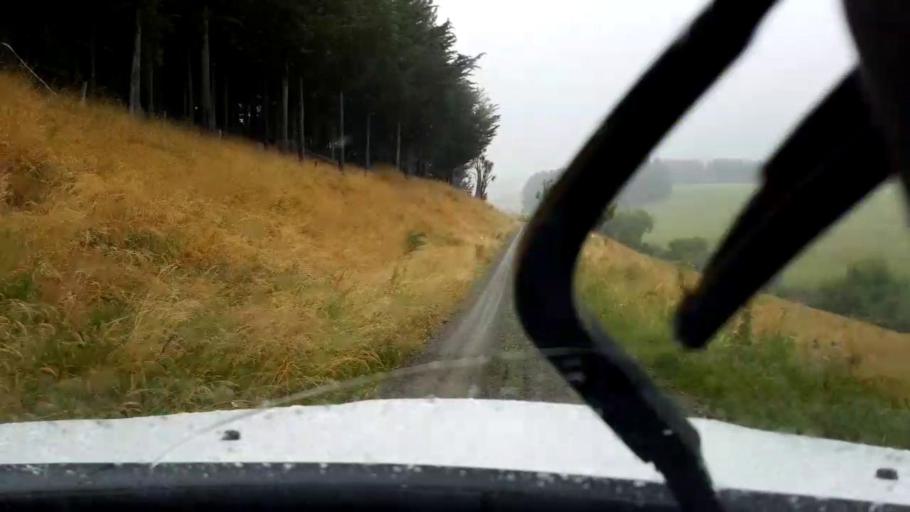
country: NZ
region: Canterbury
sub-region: Timaru District
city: Pleasant Point
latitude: -44.1877
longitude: 171.1033
